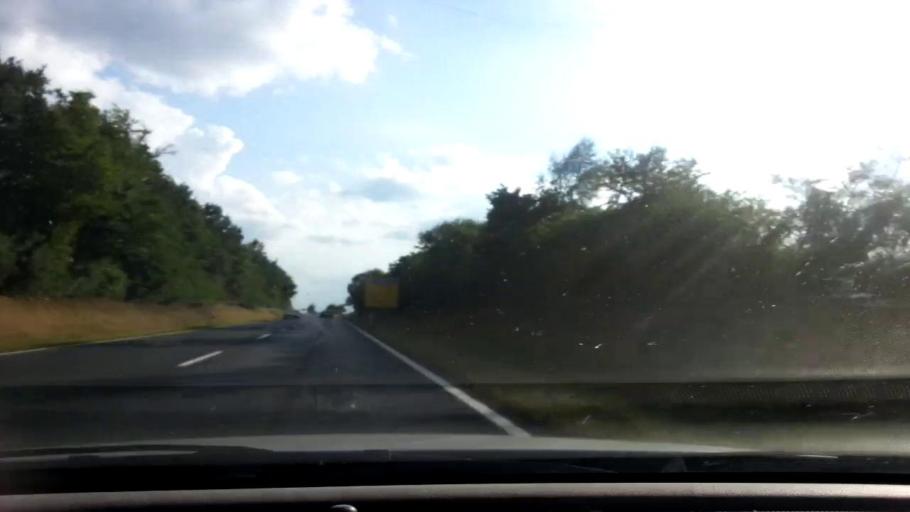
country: DE
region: Bavaria
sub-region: Upper Palatinate
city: Mitterteich
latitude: 49.9705
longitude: 12.2633
